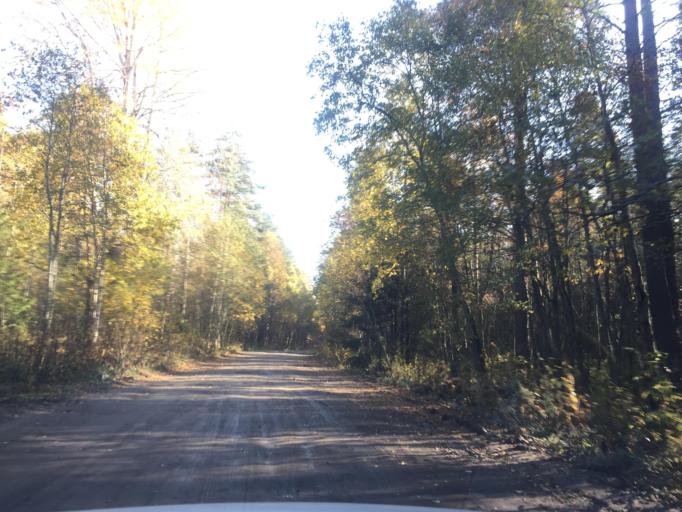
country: RU
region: Leningrad
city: Kuznechnoye
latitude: 61.3048
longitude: 30.0422
